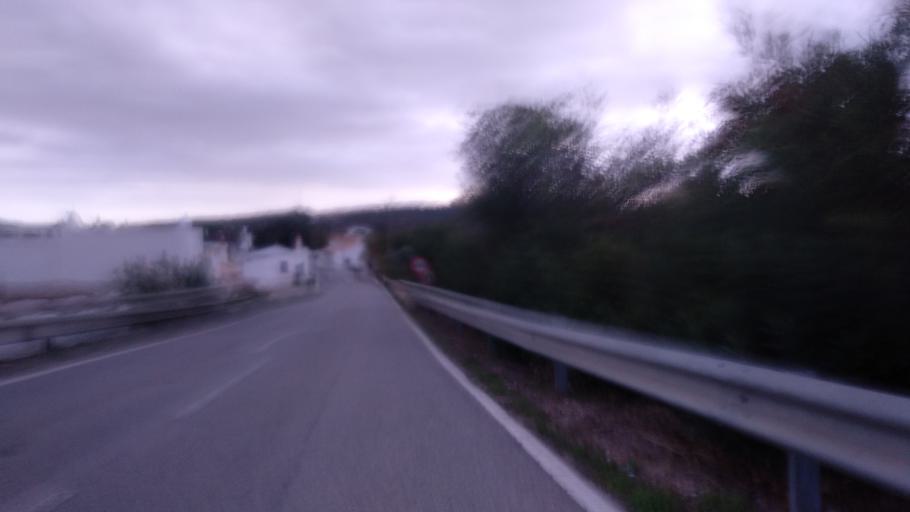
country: PT
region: Faro
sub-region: Sao Bras de Alportel
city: Sao Bras de Alportel
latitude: 37.1763
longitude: -7.9095
